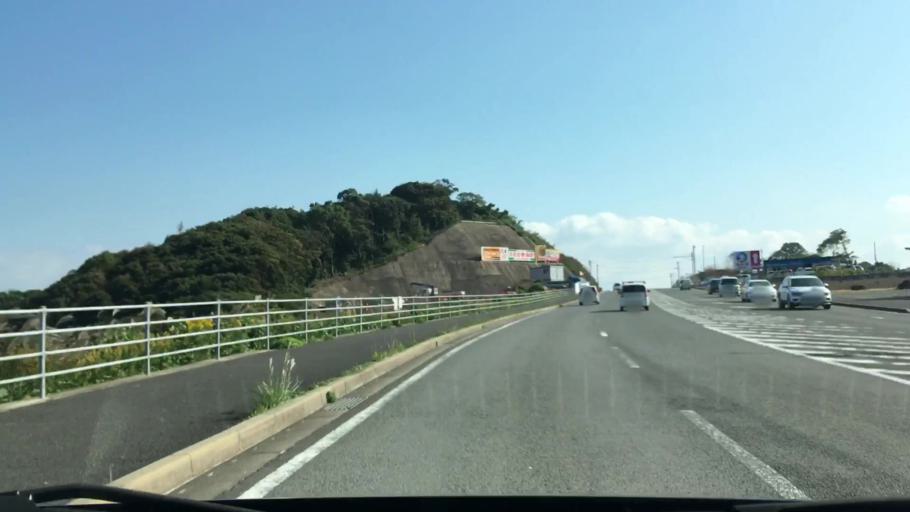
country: JP
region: Nagasaki
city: Togitsu
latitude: 32.8598
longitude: 129.8161
